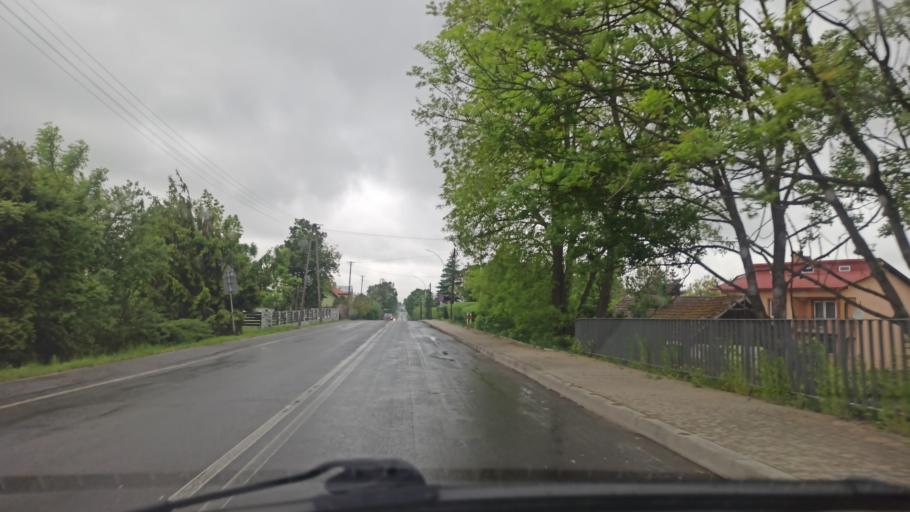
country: PL
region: Subcarpathian Voivodeship
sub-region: Powiat jaroslawski
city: Radymno
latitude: 49.9536
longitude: 22.8165
